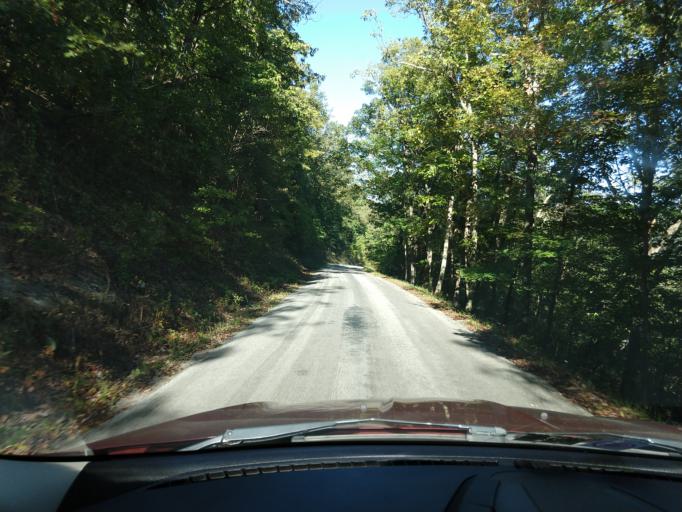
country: US
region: Virginia
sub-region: Alleghany County
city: Clifton Forge
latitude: 37.8695
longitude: -79.8817
